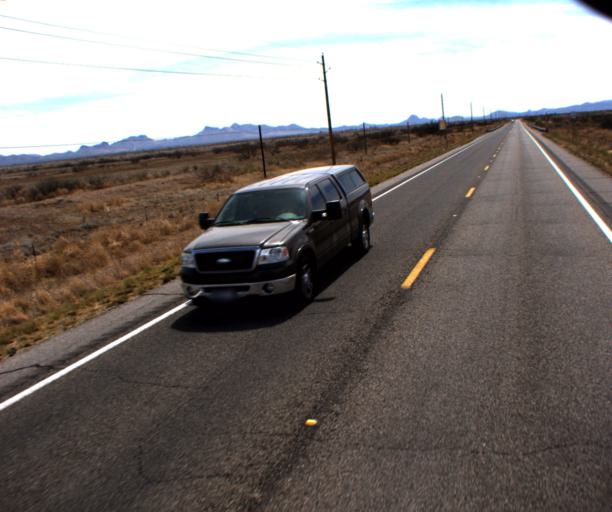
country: US
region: Arizona
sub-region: Cochise County
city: Pirtleville
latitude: 31.4432
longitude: -109.5979
